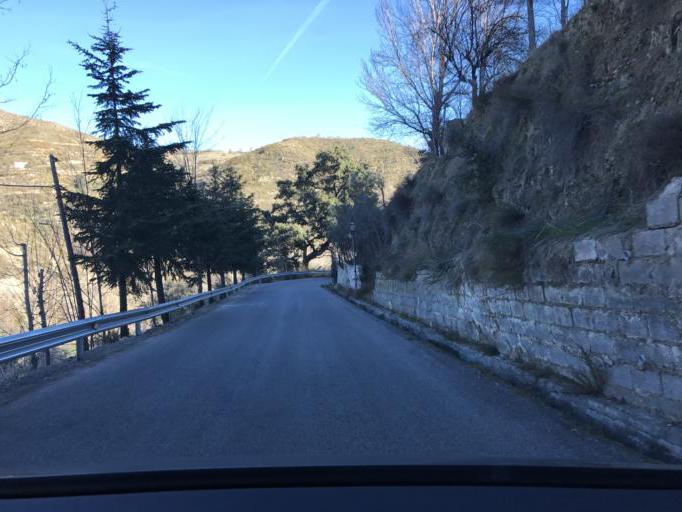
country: ES
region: Andalusia
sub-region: Provincia de Granada
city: Dudar
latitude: 37.1818
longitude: -3.4905
